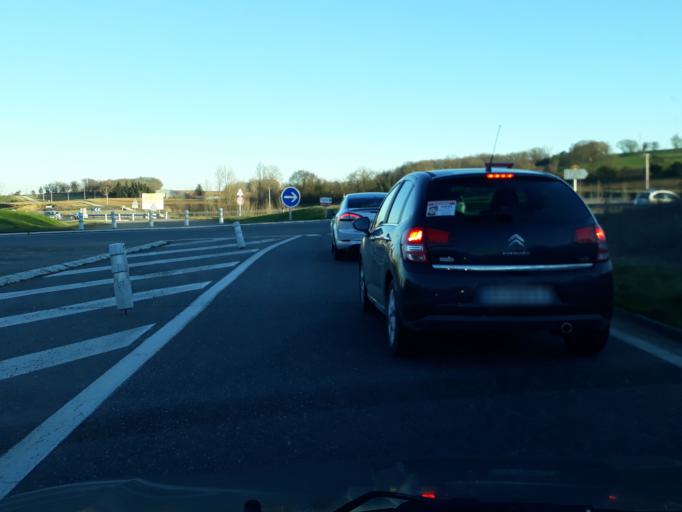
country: FR
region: Midi-Pyrenees
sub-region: Departement du Gers
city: Aubiet
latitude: 43.6382
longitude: 0.8215
